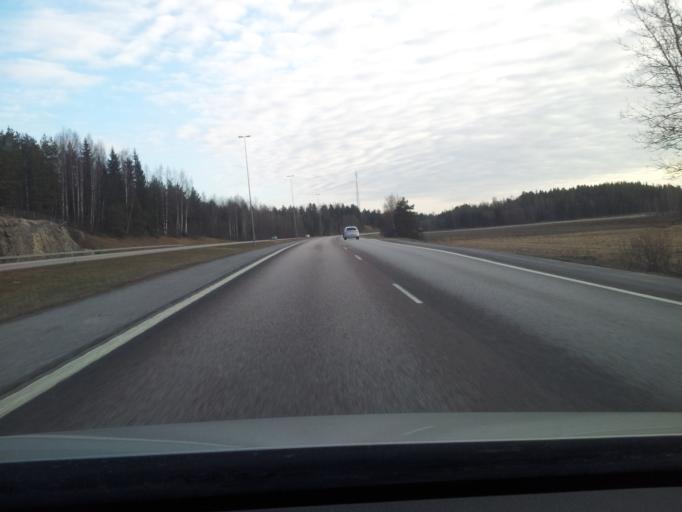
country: FI
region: Uusimaa
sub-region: Porvoo
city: Porvoo
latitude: 60.3493
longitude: 25.5166
